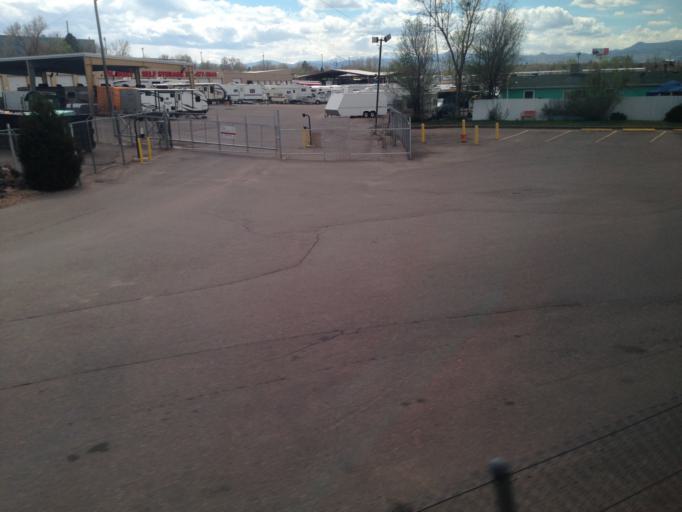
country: US
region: Colorado
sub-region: Adams County
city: Berkley
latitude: 39.8059
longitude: -105.0069
